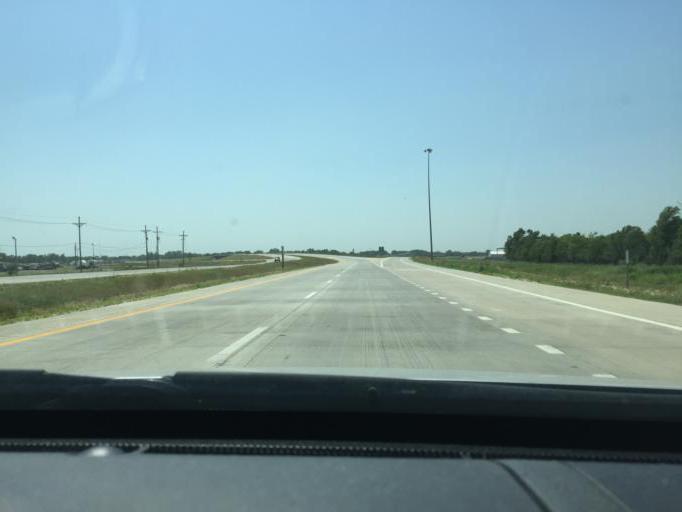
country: US
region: Kansas
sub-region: Reno County
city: South Hutchinson
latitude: 38.0290
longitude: -97.8961
